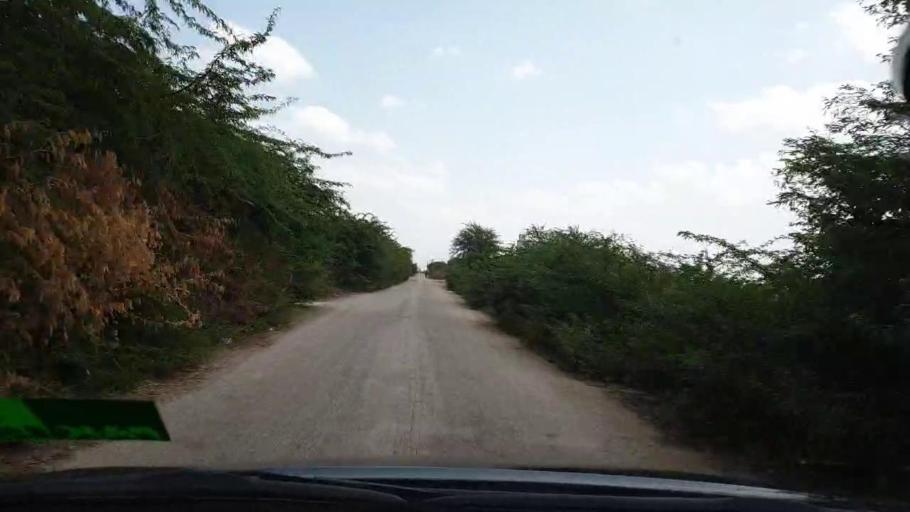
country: PK
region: Sindh
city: Kadhan
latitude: 24.6276
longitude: 69.1740
